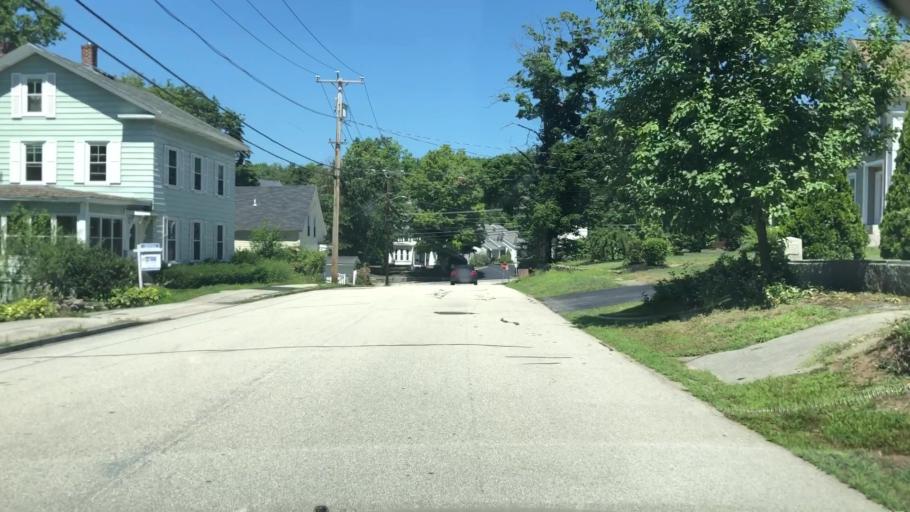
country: US
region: New Hampshire
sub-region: Hillsborough County
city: Milford
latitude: 42.8370
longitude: -71.6450
